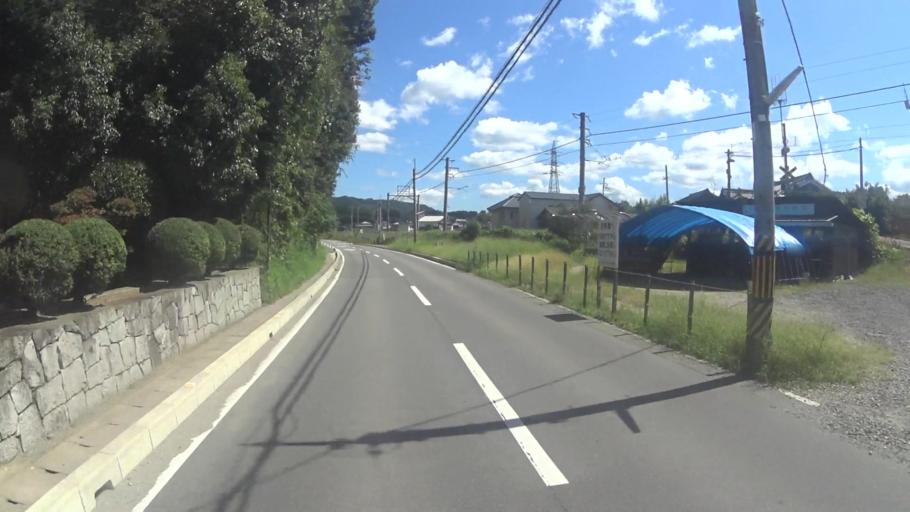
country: JP
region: Nara
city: Nara-shi
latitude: 34.7344
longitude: 135.8512
